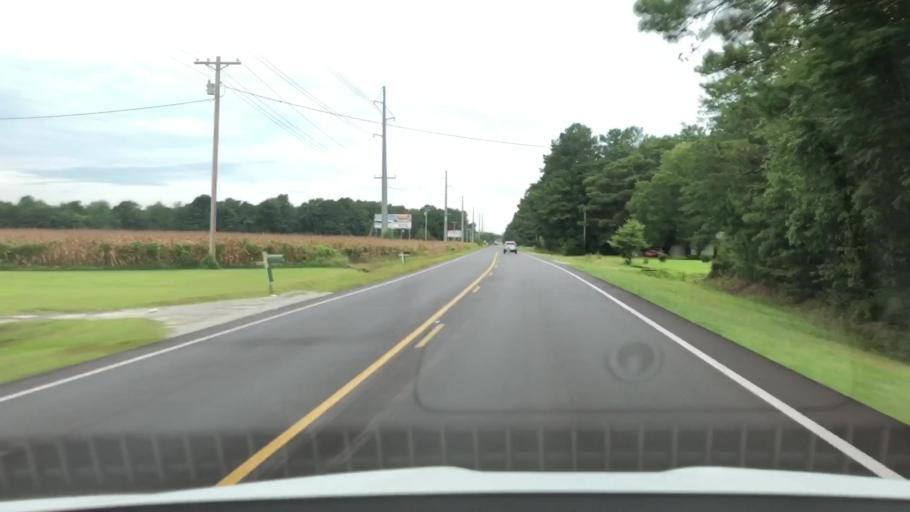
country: US
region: North Carolina
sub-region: Jones County
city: Maysville
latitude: 34.8310
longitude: -77.1606
